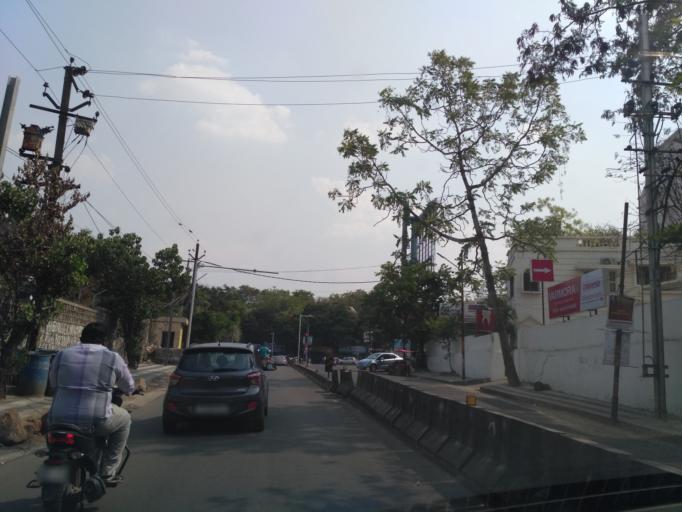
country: IN
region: Telangana
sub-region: Hyderabad
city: Hyderabad
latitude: 17.4282
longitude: 78.4397
